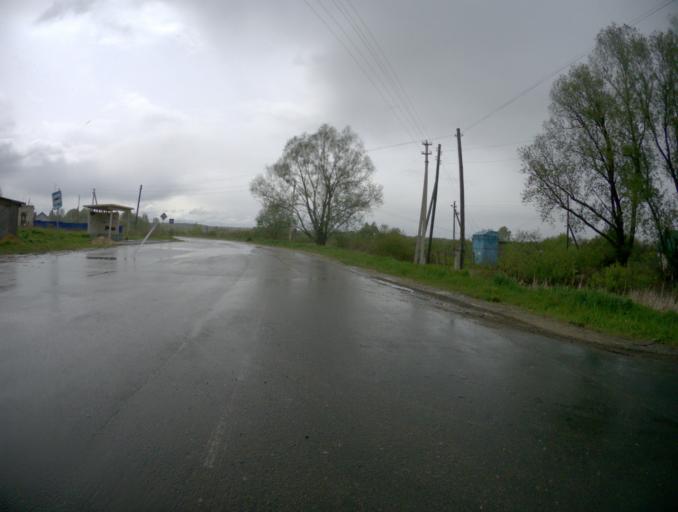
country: RU
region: Vladimir
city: Velikodvorskiy
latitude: 55.3777
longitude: 40.8096
